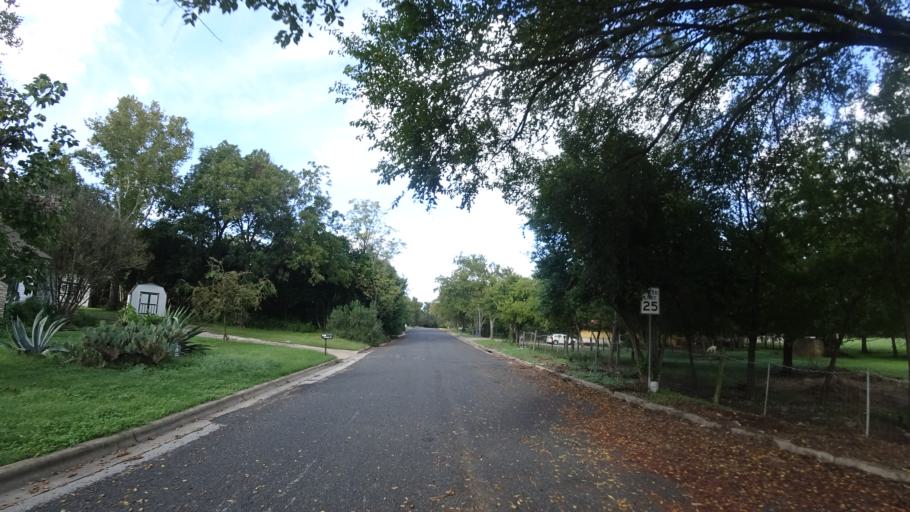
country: US
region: Texas
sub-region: Travis County
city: Onion Creek
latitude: 30.2049
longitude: -97.8011
